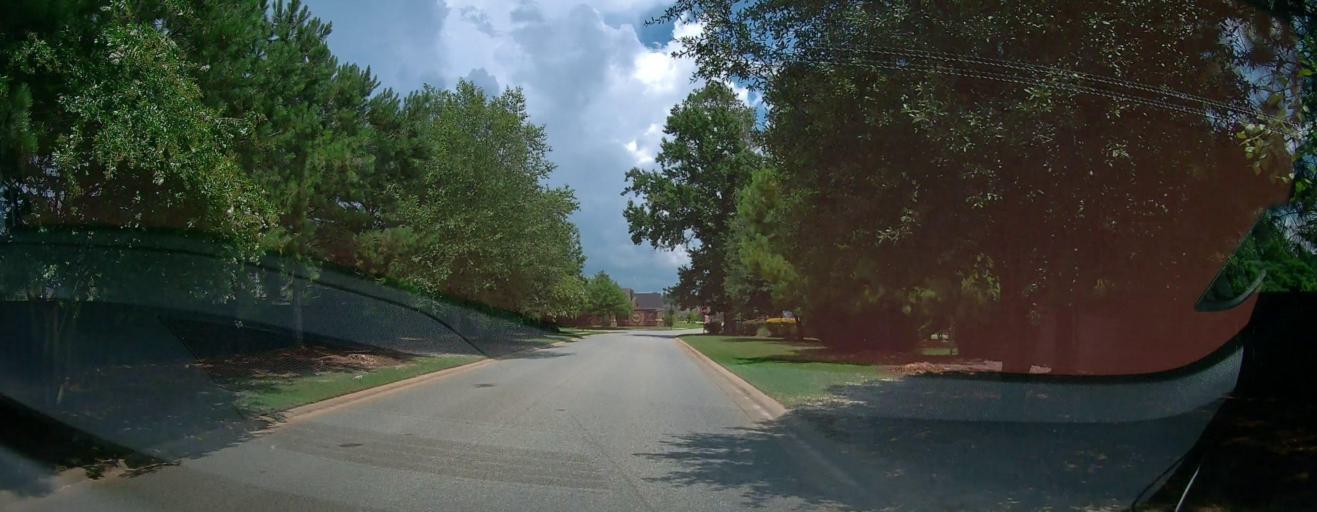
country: US
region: Georgia
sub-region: Houston County
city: Perry
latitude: 32.5098
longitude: -83.6362
